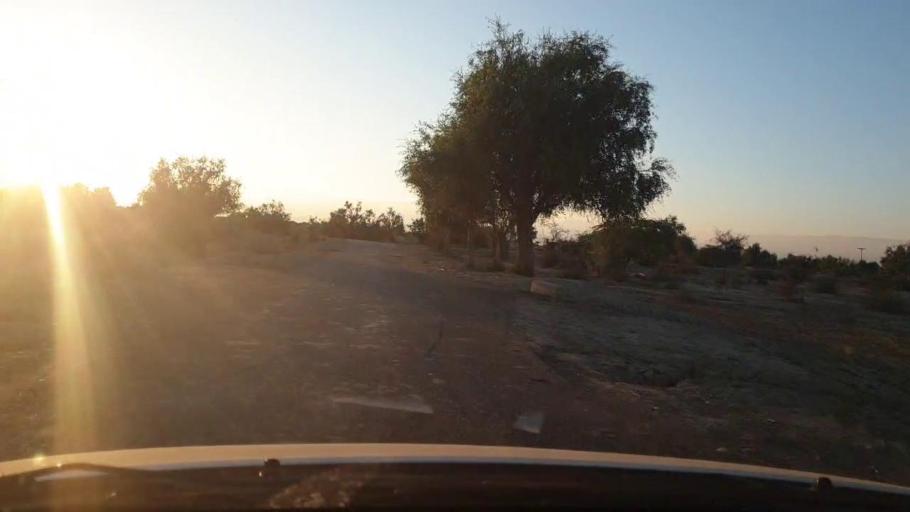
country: PK
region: Sindh
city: Johi
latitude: 26.8296
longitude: 67.4647
